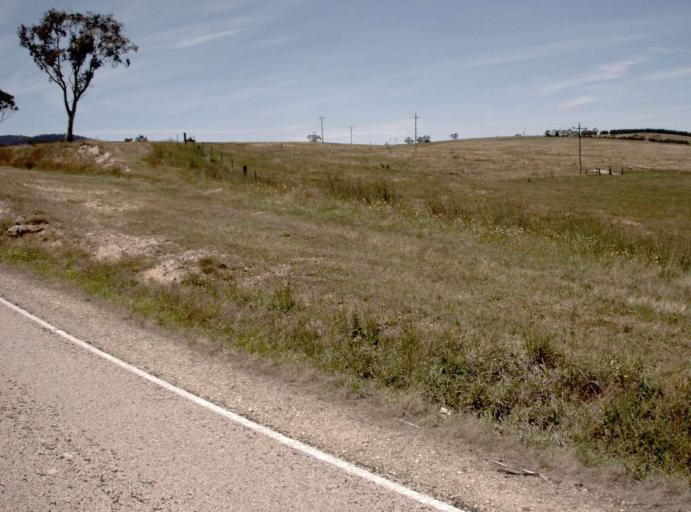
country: AU
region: Victoria
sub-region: Alpine
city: Mount Beauty
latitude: -37.1213
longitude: 147.6305
